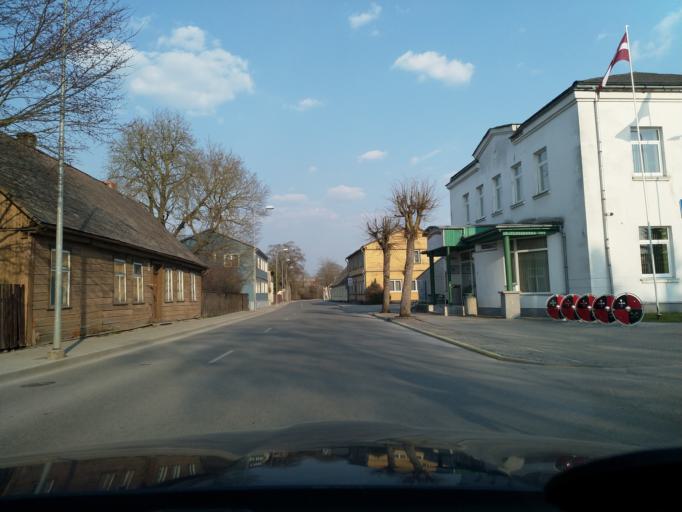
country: LV
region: Grobina
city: Grobina
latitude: 56.5352
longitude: 21.1691
